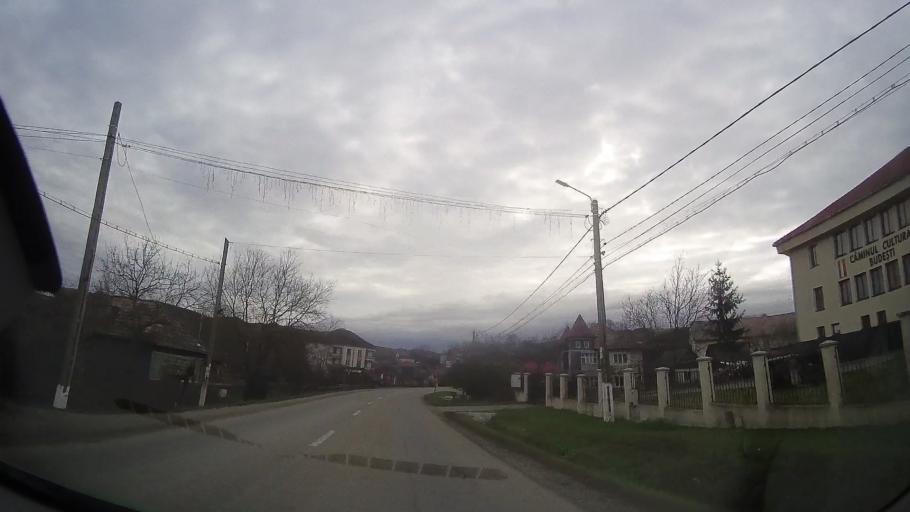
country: RO
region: Bistrita-Nasaud
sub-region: Comuna Budesti
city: Budesti
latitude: 46.8775
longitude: 24.2423
